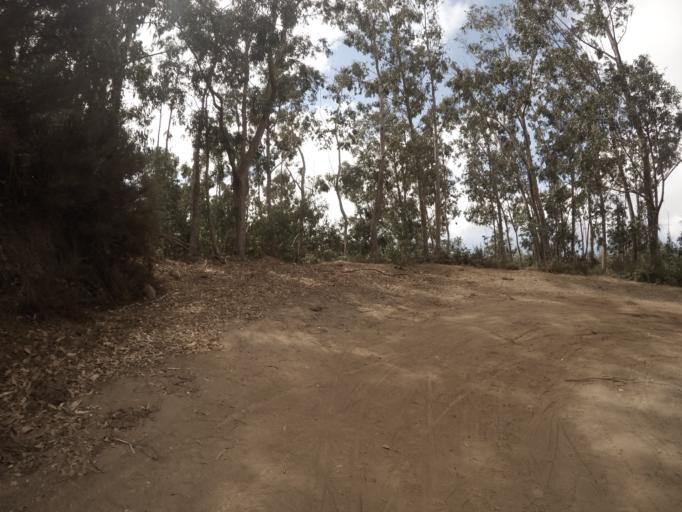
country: PT
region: Madeira
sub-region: Camara de Lobos
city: Curral das Freiras
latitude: 32.7093
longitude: -17.0096
